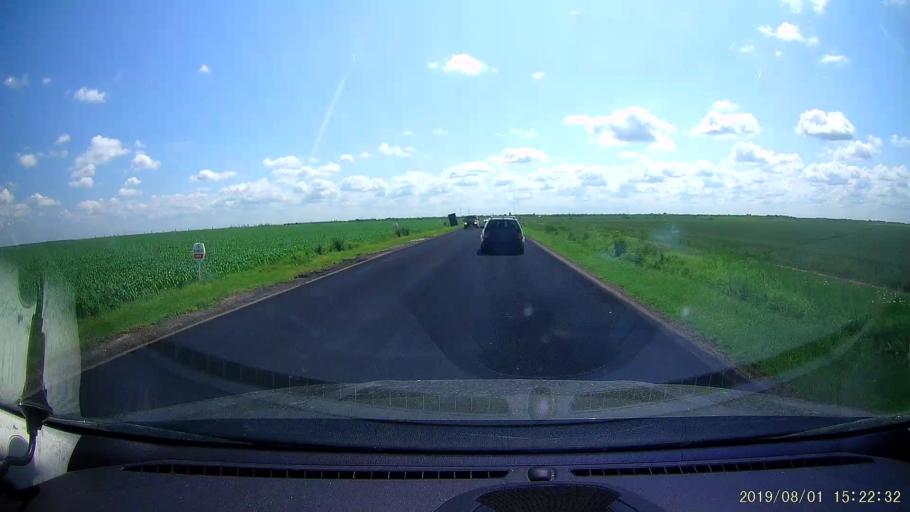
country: RO
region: Braila
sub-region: Comuna Viziru
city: Lanurile
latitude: 45.0523
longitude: 27.7745
